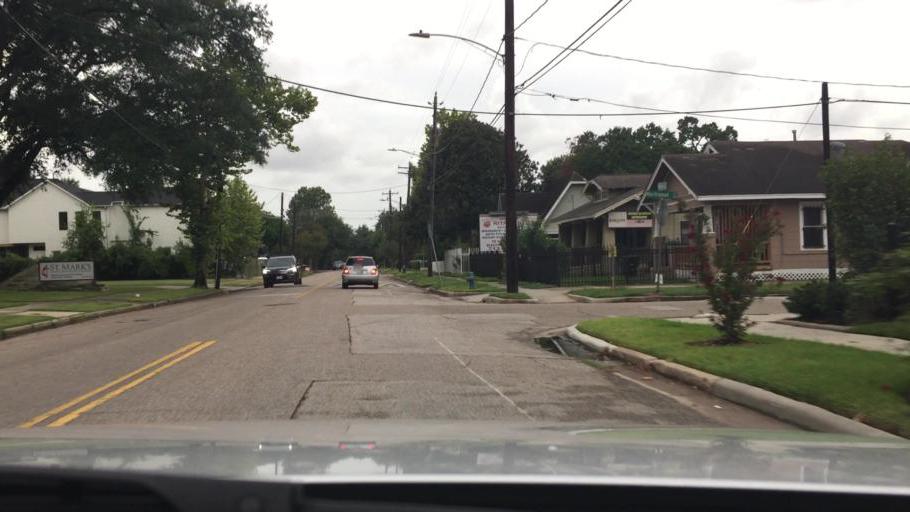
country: US
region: Texas
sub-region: Harris County
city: Houston
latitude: 29.7906
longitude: -95.3775
